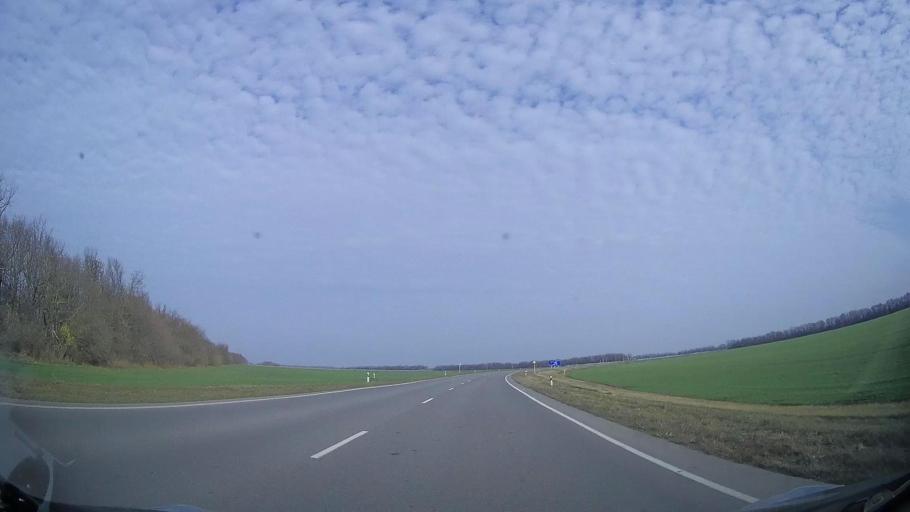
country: RU
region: Rostov
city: Tselina
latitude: 46.5218
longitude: 41.0738
